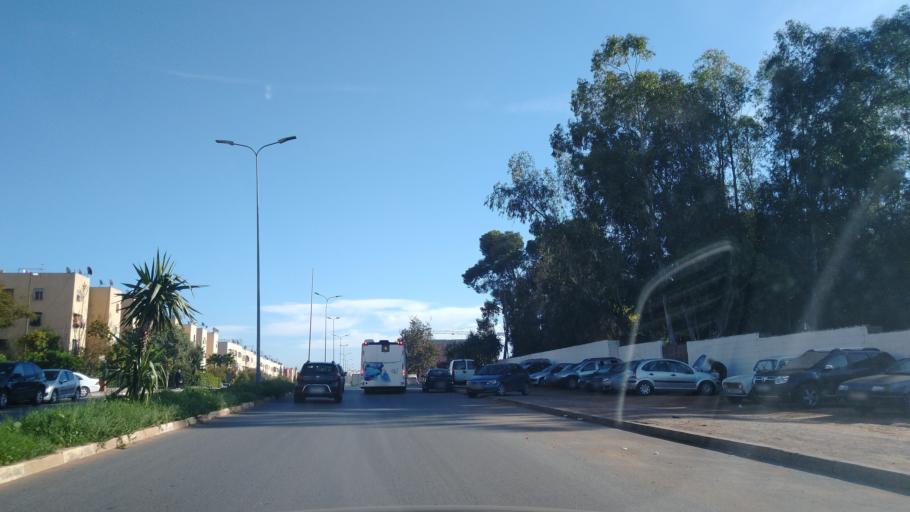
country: MA
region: Rabat-Sale-Zemmour-Zaer
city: Sale
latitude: 33.9979
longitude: -6.7486
